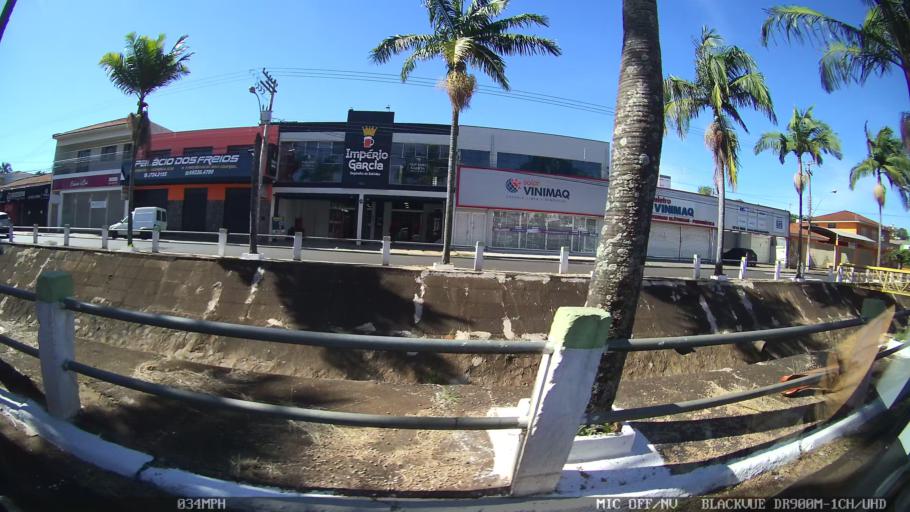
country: BR
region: Sao Paulo
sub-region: Franca
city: Franca
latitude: -20.5244
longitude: -47.4013
